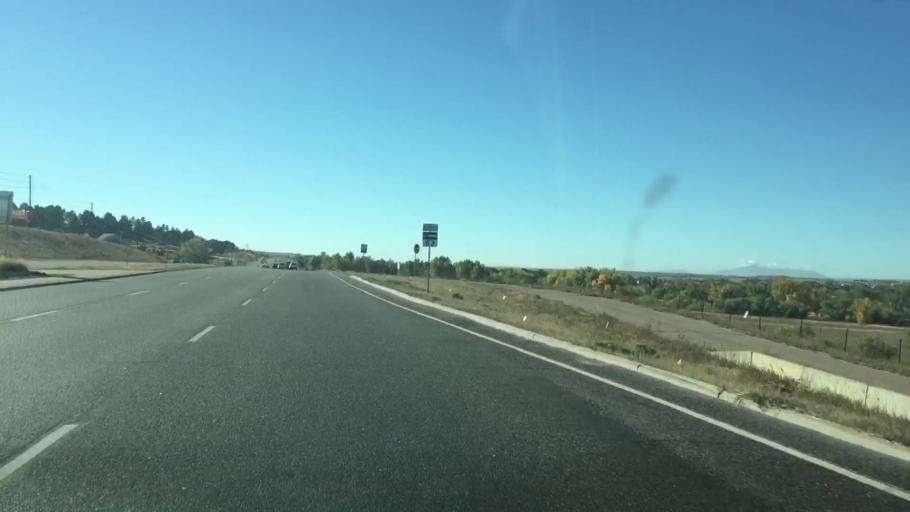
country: US
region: Colorado
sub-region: Douglas County
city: Parker
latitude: 39.5073
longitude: -104.7635
